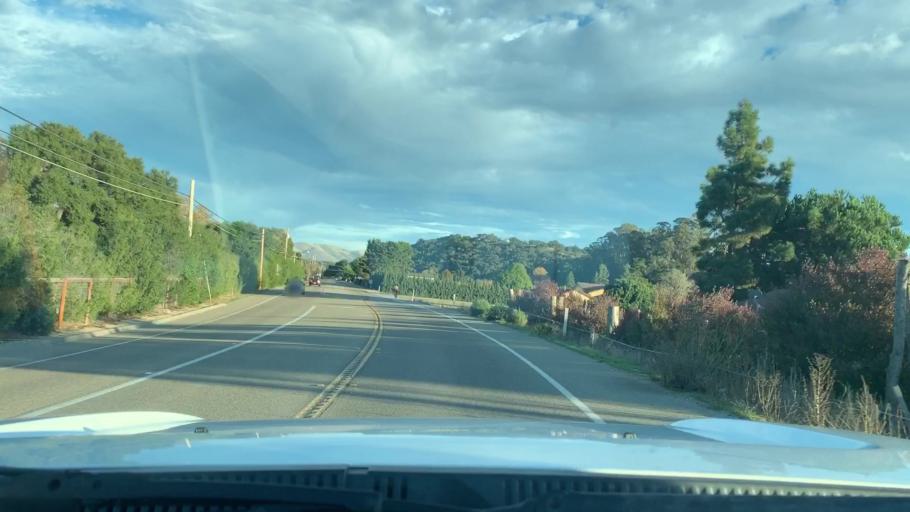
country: US
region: California
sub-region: San Luis Obispo County
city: Callender
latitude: 35.0794
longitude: -120.5467
